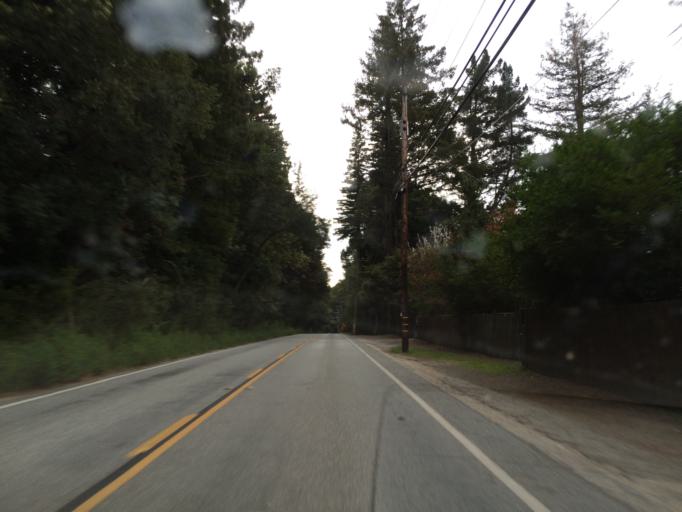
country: US
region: California
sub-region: Santa Cruz County
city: Brookdale
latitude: 37.0813
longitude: -122.1345
